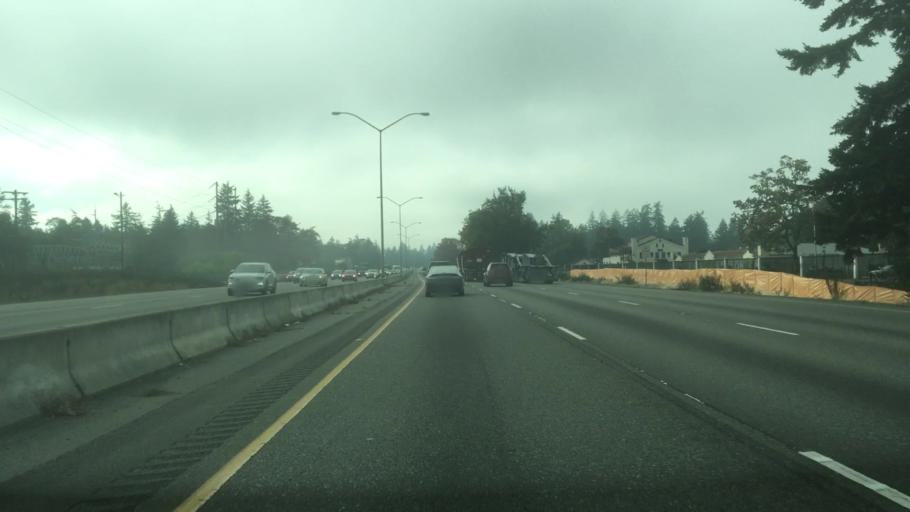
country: US
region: Washington
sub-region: Pierce County
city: Fort Lewis
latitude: 47.1161
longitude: -122.5615
